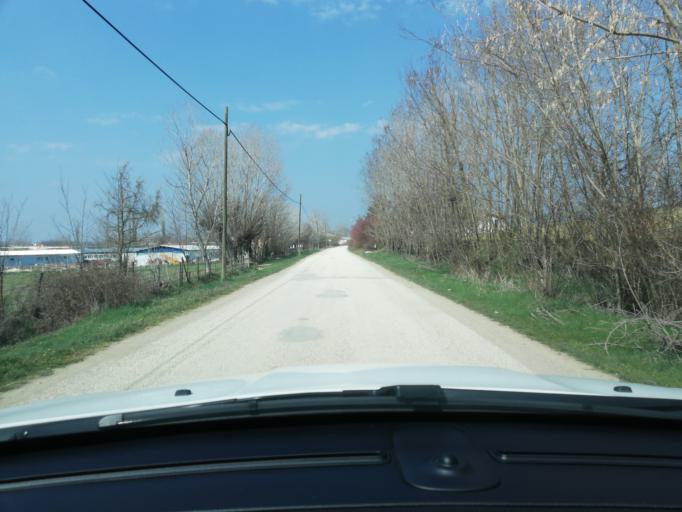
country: TR
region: Kastamonu
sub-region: Cide
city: Kastamonu
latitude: 41.4575
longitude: 33.7667
